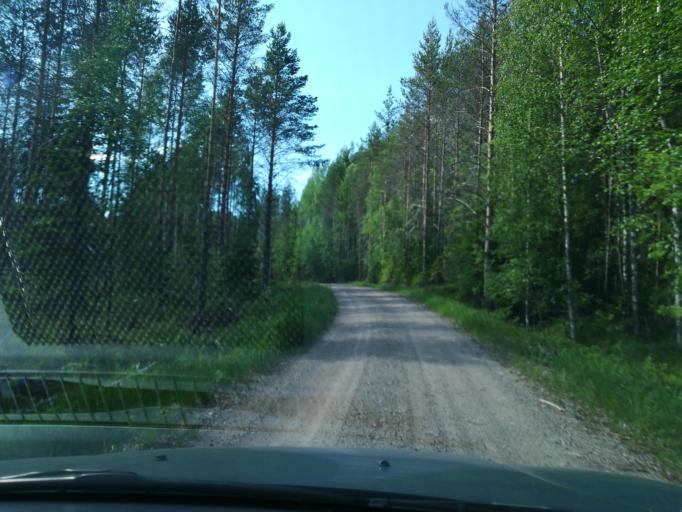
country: FI
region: South Karelia
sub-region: Imatra
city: Ruokolahti
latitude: 61.5375
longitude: 28.8300
